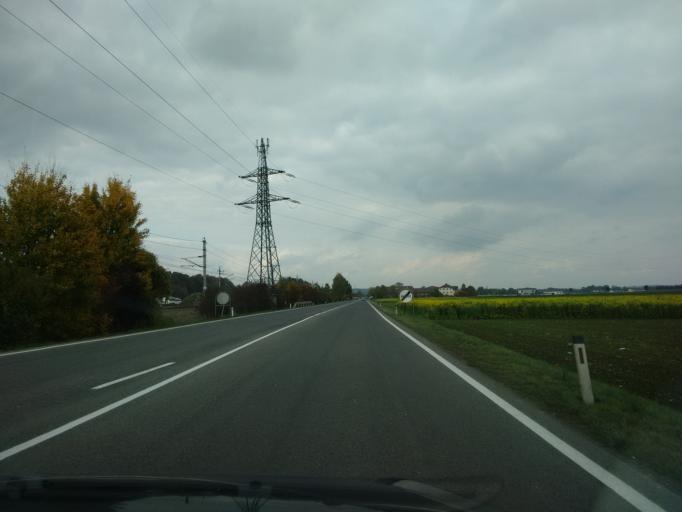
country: AT
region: Upper Austria
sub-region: Politischer Bezirk Vocklabruck
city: Redlham
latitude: 48.0287
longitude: 13.7364
